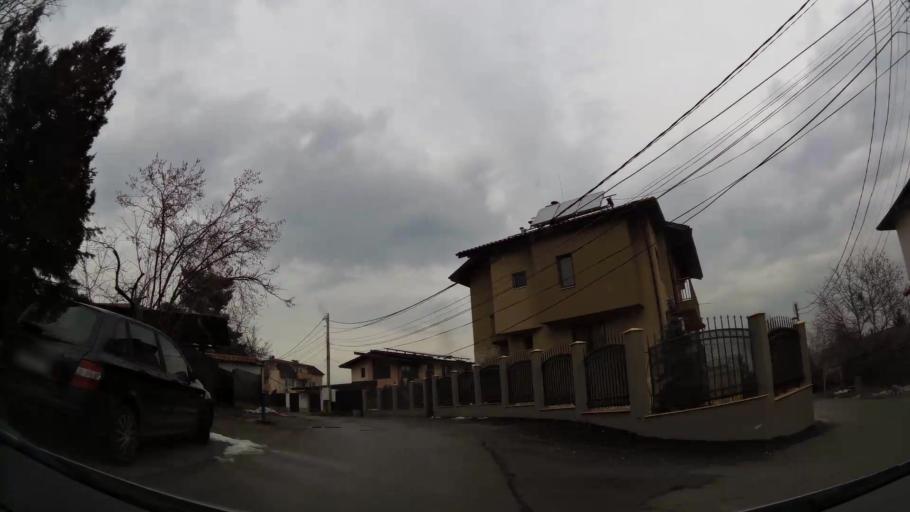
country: BG
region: Sofiya
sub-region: Obshtina Bozhurishte
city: Bozhurishte
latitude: 42.6821
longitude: 23.2344
